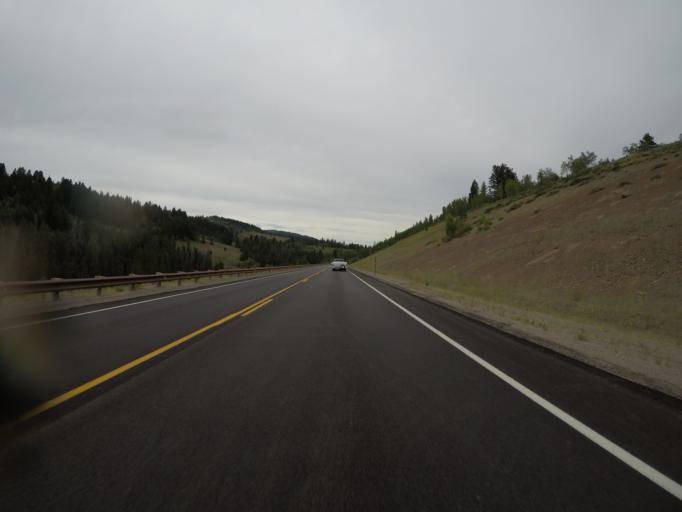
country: US
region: Wyoming
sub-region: Lincoln County
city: Afton
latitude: 42.5346
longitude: -110.8989
